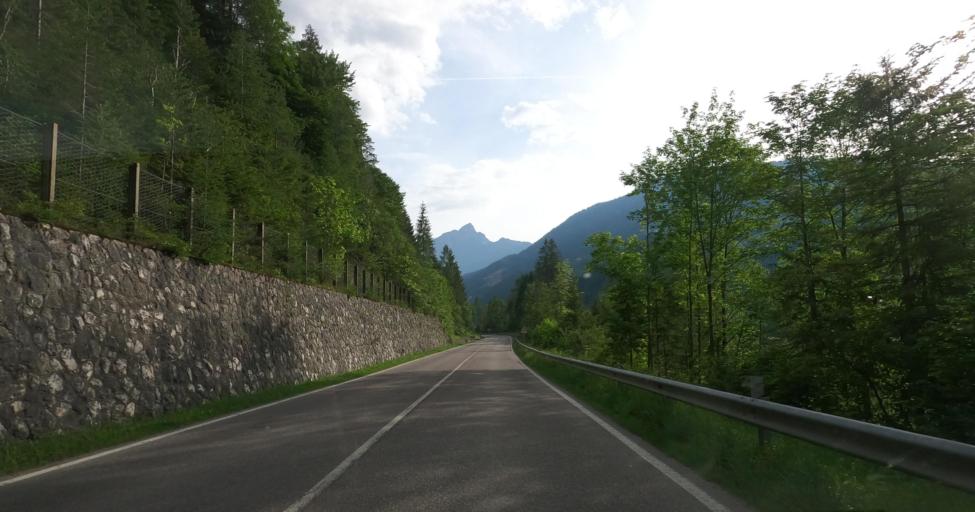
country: IT
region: Veneto
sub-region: Provincia di Belluno
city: Celat-San Tomaso Agordino
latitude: 46.3821
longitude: 11.9898
